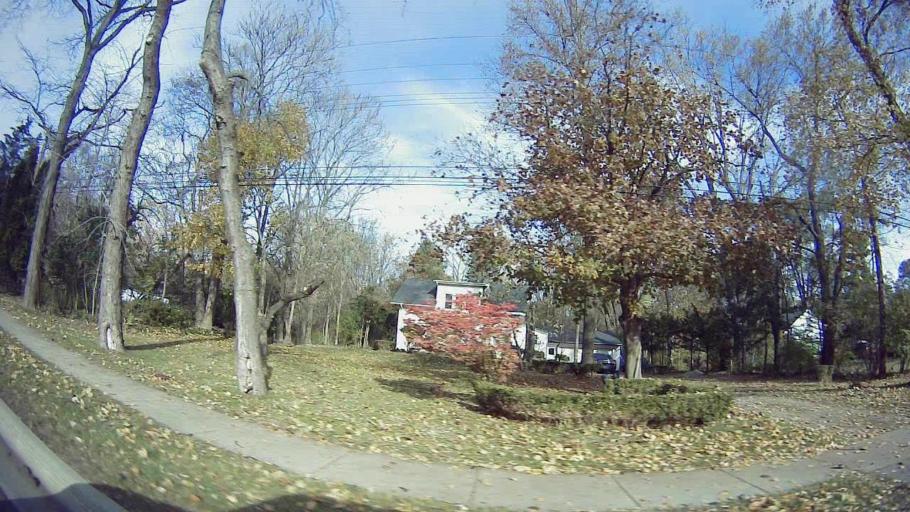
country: US
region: Michigan
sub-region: Oakland County
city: Southfield
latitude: 42.4580
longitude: -83.2523
